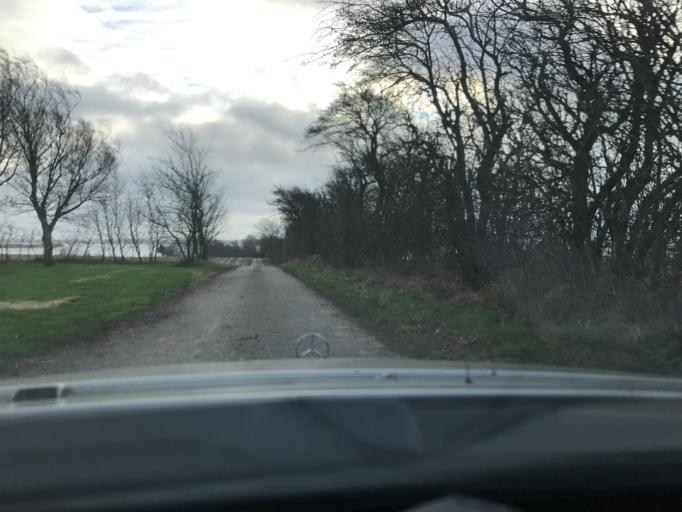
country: DK
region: South Denmark
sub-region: Sonderborg Kommune
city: Nordborg
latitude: 55.0434
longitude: 9.6535
